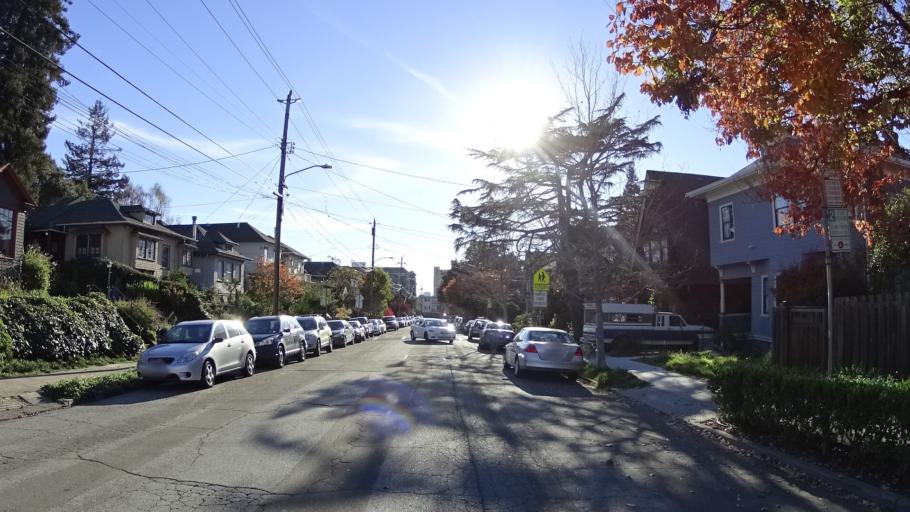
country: US
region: California
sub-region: Alameda County
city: Piedmont
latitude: 37.8294
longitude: -122.2535
